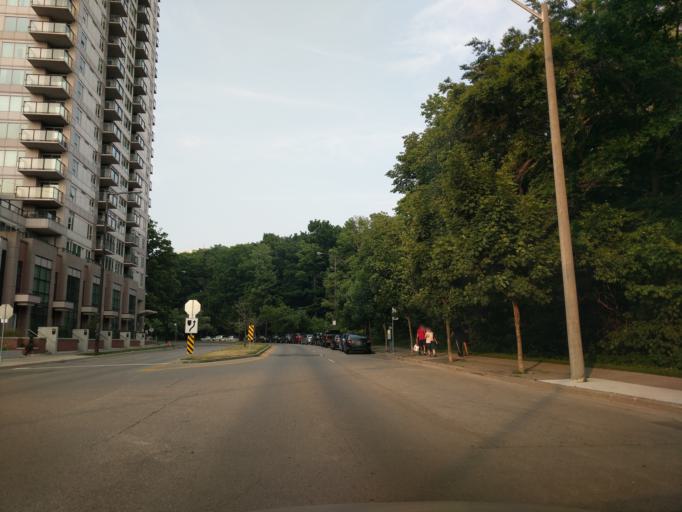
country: CA
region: Ontario
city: Scarborough
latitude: 43.7725
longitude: -79.2547
